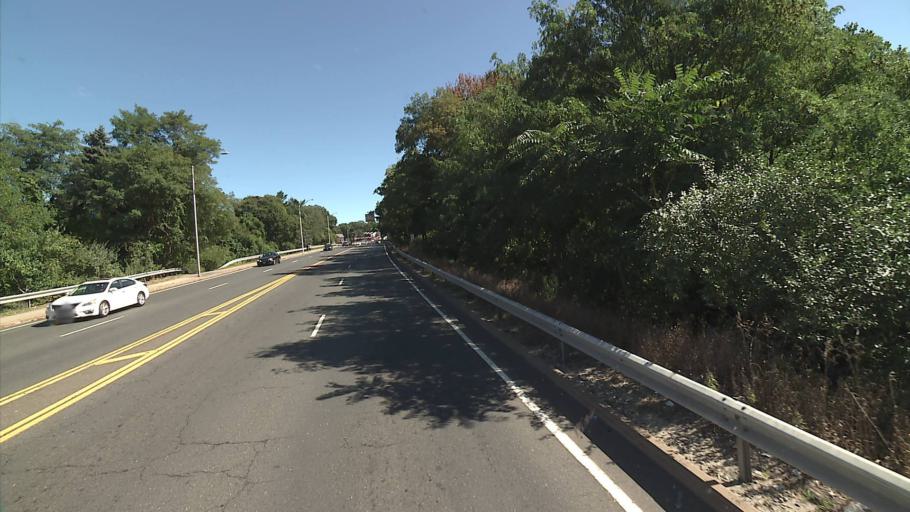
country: US
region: Connecticut
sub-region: New Haven County
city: Waterbury
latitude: 41.5461
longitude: -73.0213
